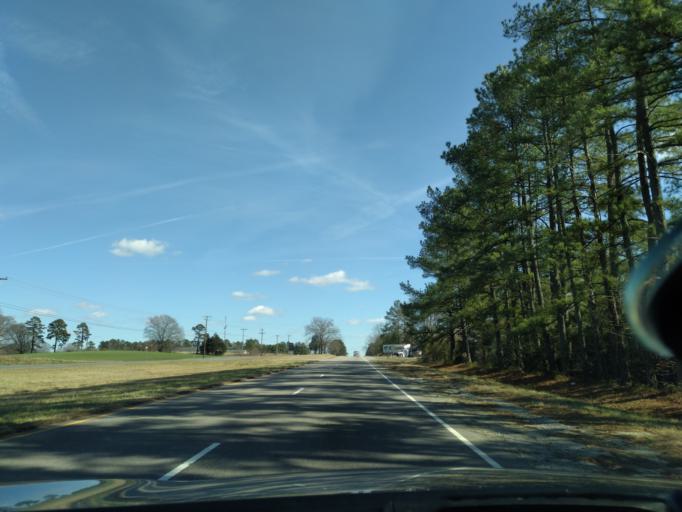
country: US
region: Virginia
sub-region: Nottoway County
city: Crewe
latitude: 37.1900
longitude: -78.1646
